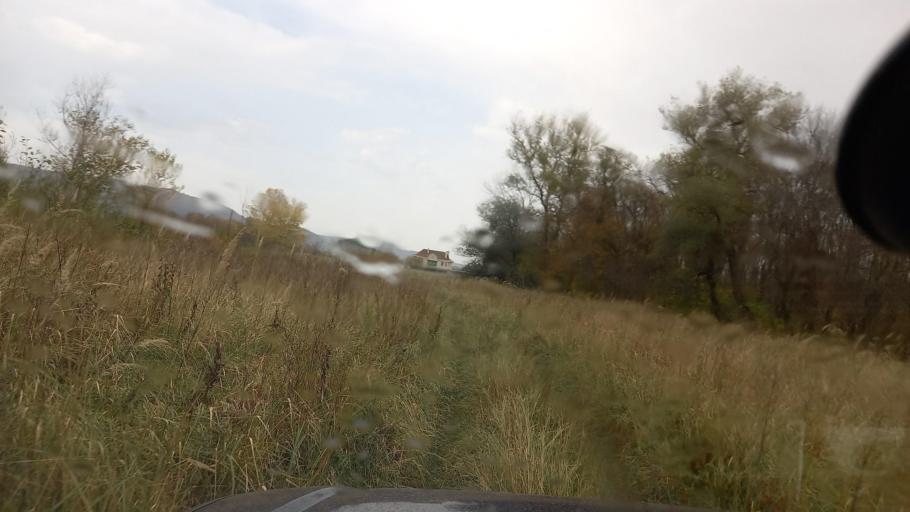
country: RU
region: Krasnodarskiy
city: Shedok
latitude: 44.1723
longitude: 40.8446
